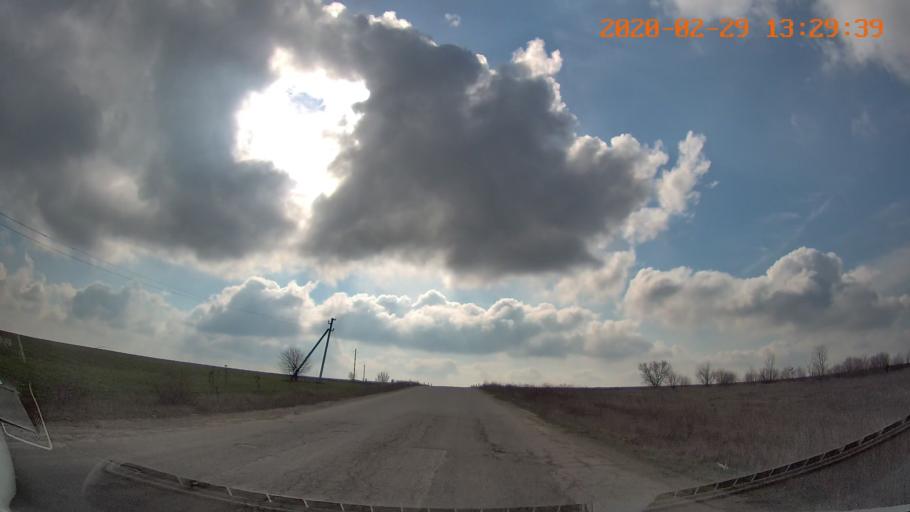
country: MD
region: Telenesti
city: Camenca
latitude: 47.8948
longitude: 28.6349
